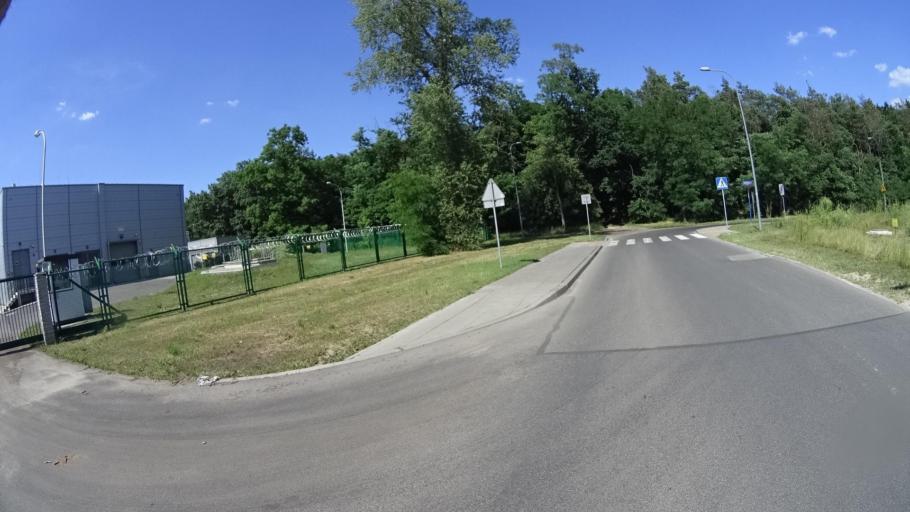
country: PL
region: Masovian Voivodeship
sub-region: Warszawa
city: Bialoleka
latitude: 52.3524
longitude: 20.9674
